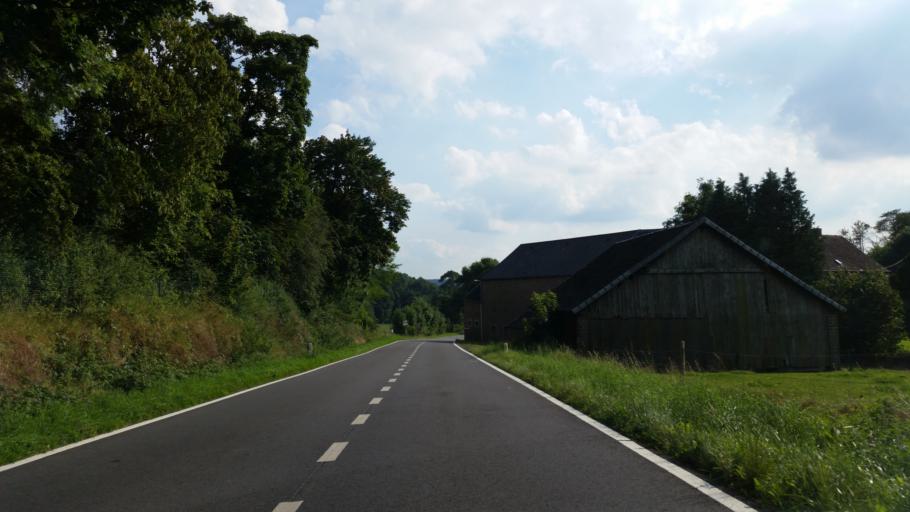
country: BE
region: Wallonia
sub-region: Province de Liege
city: Ouffet
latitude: 50.4331
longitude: 5.4578
